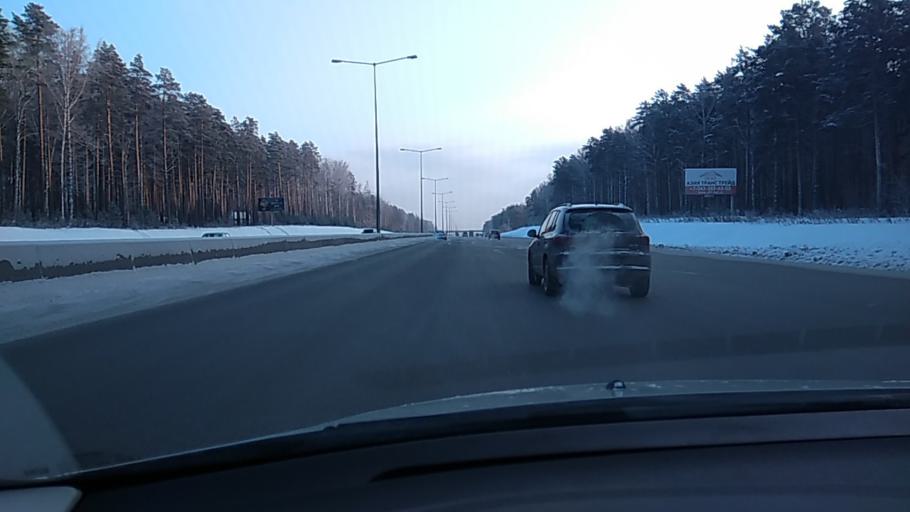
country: RU
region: Sverdlovsk
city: Istok
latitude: 56.7861
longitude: 60.6852
